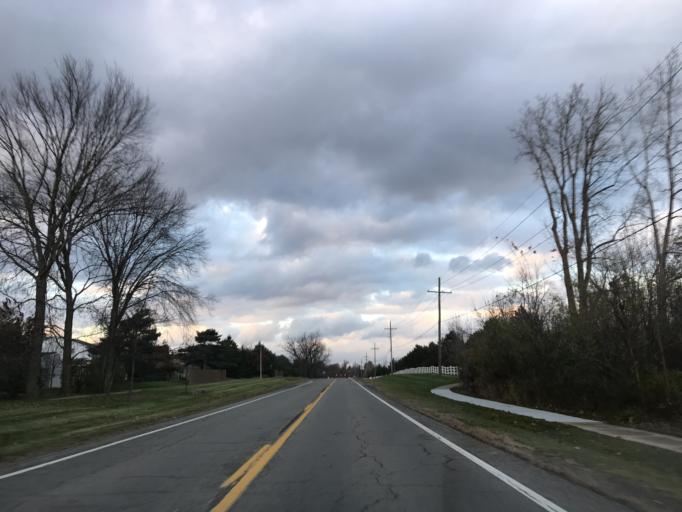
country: US
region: Michigan
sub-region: Oakland County
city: South Lyon
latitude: 42.4707
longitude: -83.6372
